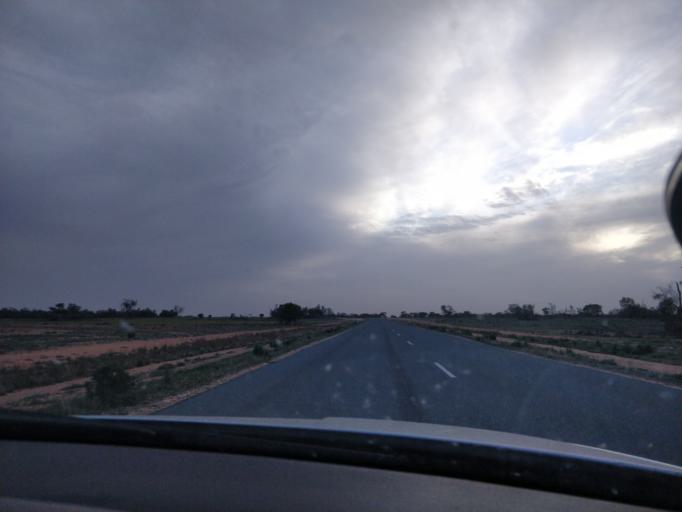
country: AU
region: New South Wales
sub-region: Wentworth
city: Gol Gol
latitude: -34.0362
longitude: 142.3637
